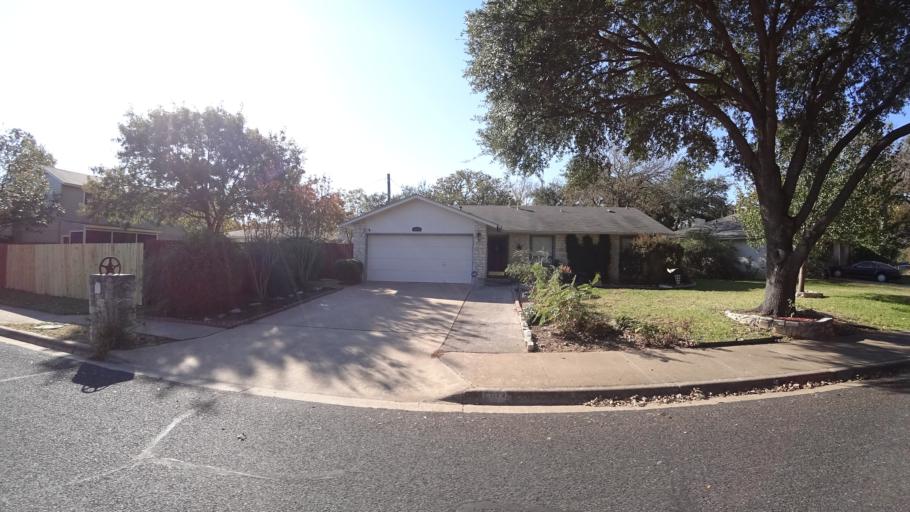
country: US
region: Texas
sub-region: Travis County
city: Barton Creek
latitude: 30.2288
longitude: -97.8468
